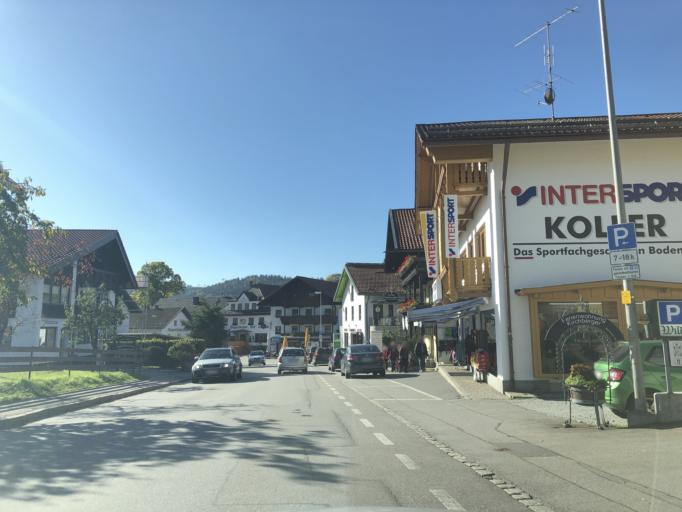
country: DE
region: Bavaria
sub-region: Lower Bavaria
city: Bodenmais
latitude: 49.0690
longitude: 13.1033
